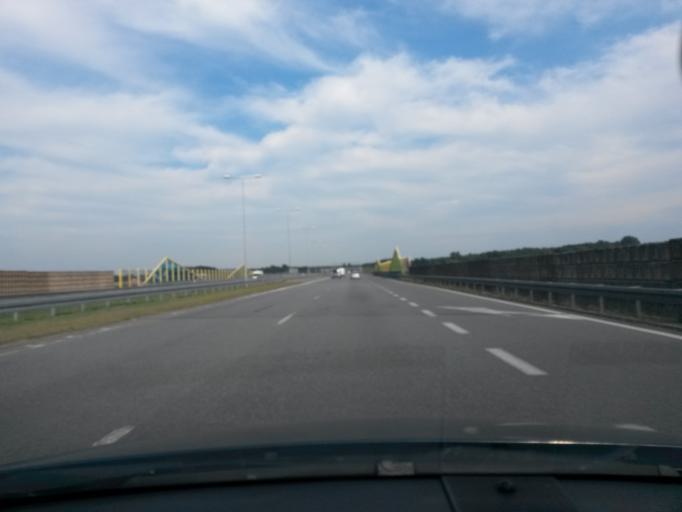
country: PL
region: Greater Poland Voivodeship
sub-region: Powiat koninski
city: Stare Miasto
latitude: 52.1620
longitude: 18.2150
